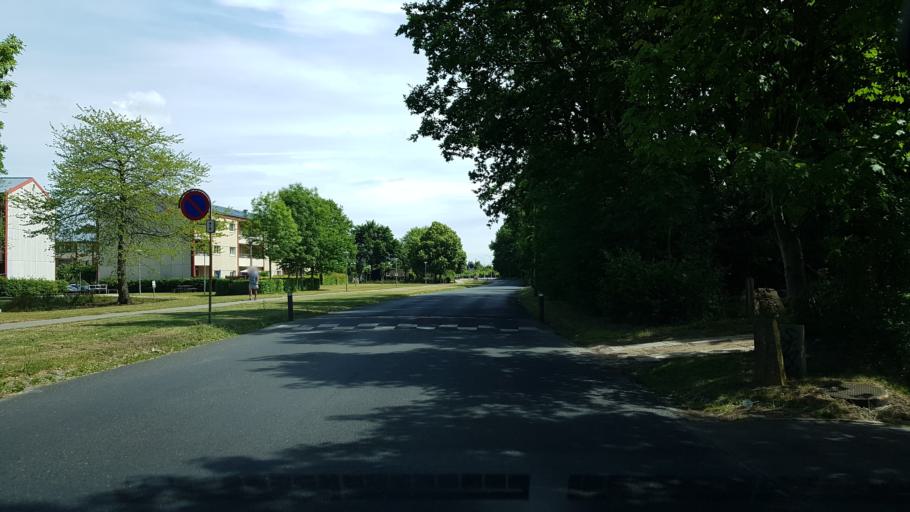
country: DK
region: Capital Region
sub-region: Rodovre Kommune
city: Rodovre
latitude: 55.6652
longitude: 12.4510
